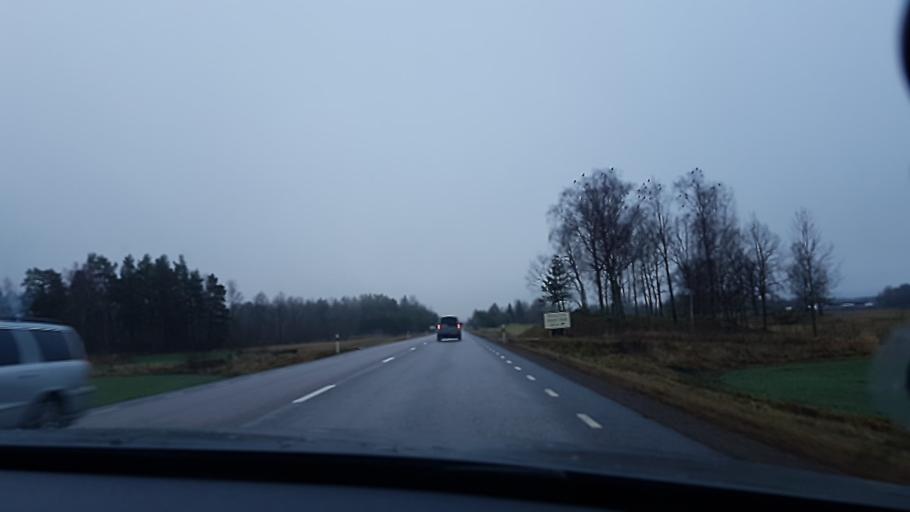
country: SE
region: Vaestra Goetaland
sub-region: Toreboda Kommun
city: Toereboda
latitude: 58.8081
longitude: 13.9770
